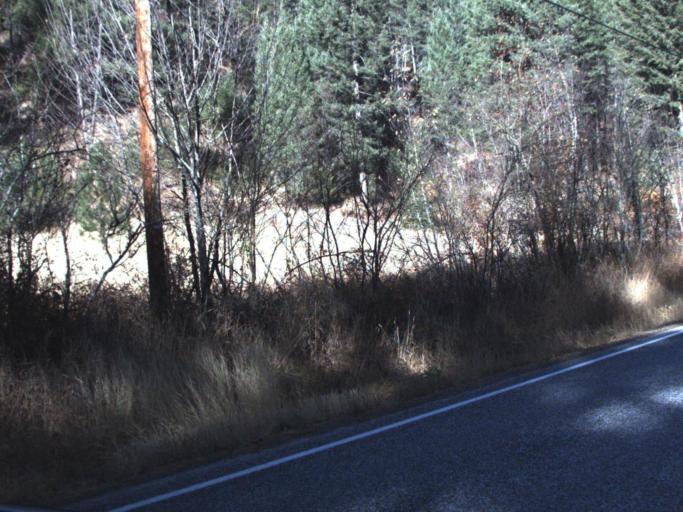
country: CA
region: British Columbia
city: Grand Forks
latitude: 48.9764
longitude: -118.5269
